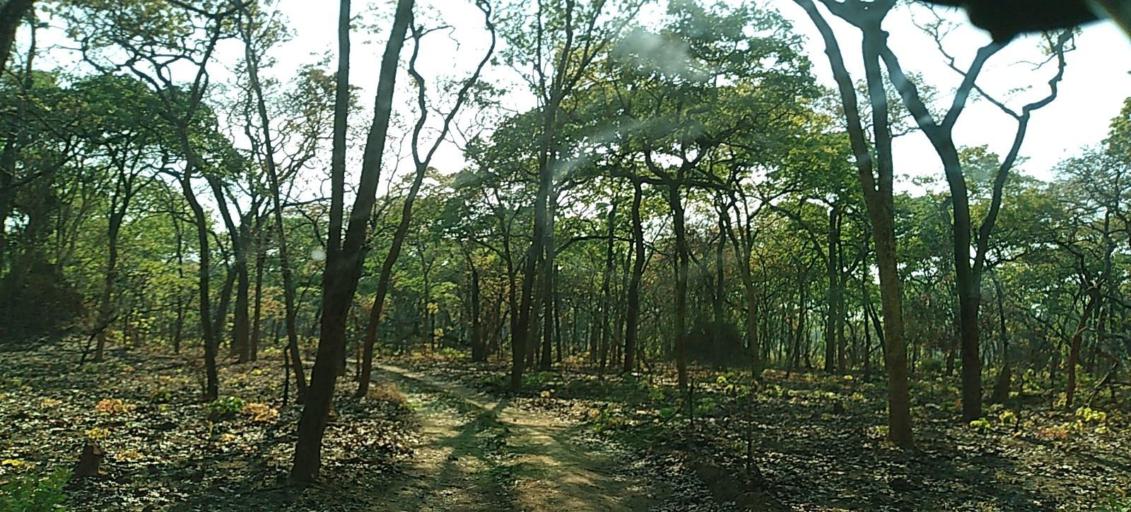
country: ZM
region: North-Western
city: Kalengwa
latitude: -13.2334
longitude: 25.0717
